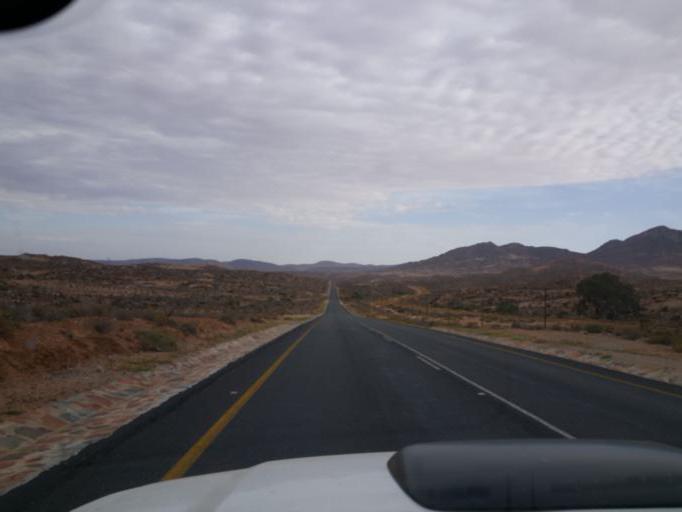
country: ZA
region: Northern Cape
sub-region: Namakwa District Municipality
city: Springbok
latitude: -29.5453
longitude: 17.8645
